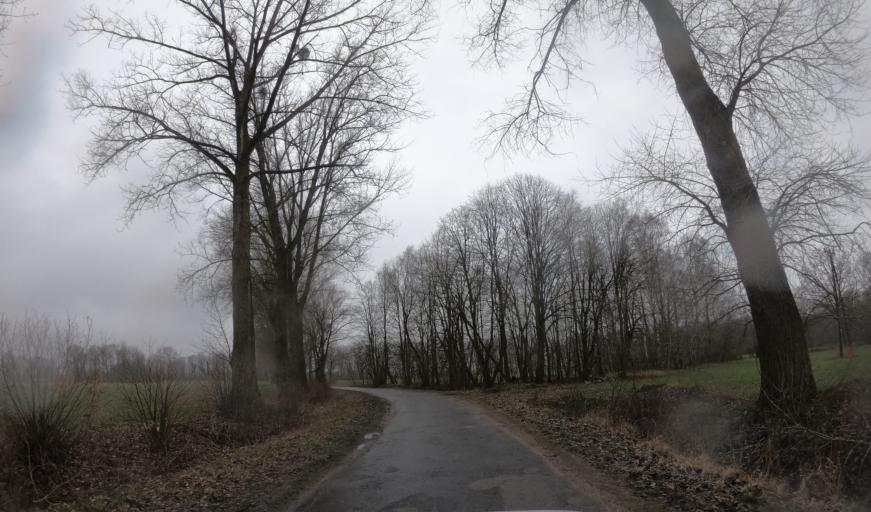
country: PL
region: West Pomeranian Voivodeship
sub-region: Powiat kamienski
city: Kamien Pomorski
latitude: 53.9072
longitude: 14.8327
